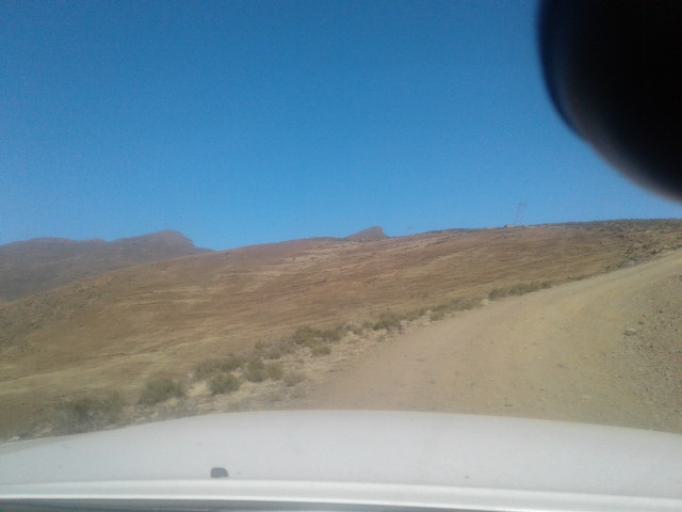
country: LS
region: Maseru
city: Nako
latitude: -29.3899
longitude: 28.0060
